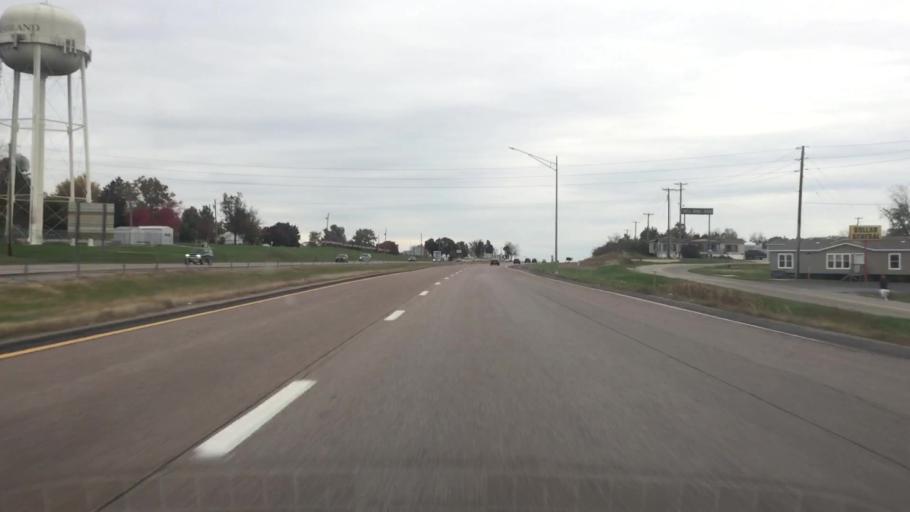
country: US
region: Missouri
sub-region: Boone County
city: Ashland
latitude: 38.7776
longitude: -92.2522
